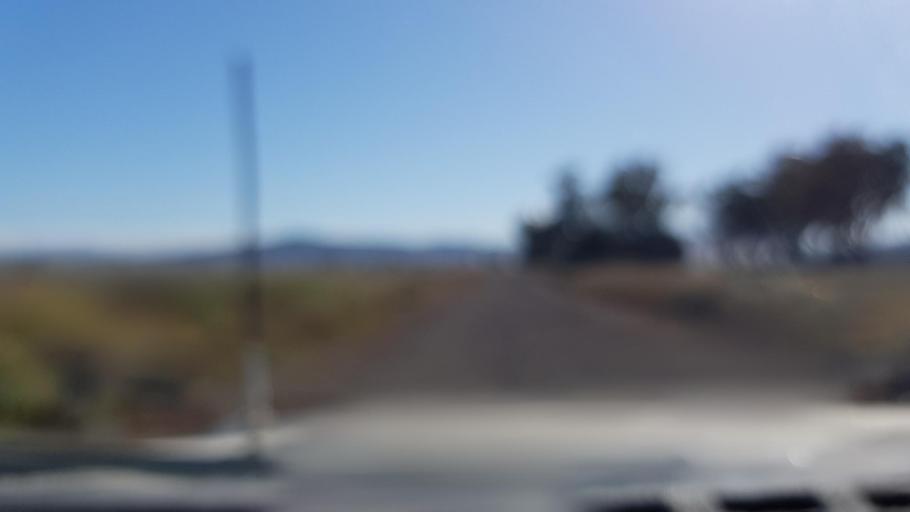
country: AU
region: New South Wales
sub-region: Narrabri
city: Blair Athol
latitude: -30.7227
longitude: 150.2863
